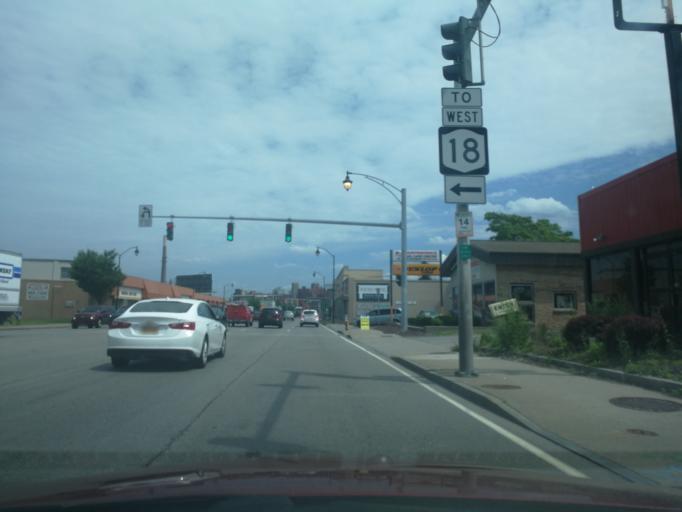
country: US
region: New York
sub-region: Monroe County
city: Rochester
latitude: 43.2012
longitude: -77.6408
